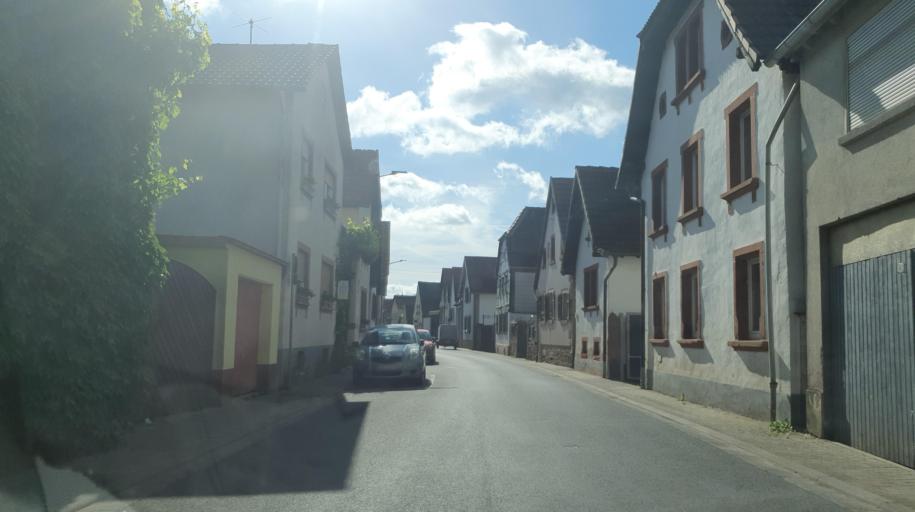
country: DE
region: Rheinland-Pfalz
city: Gocklingen
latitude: 49.1624
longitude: 8.0361
